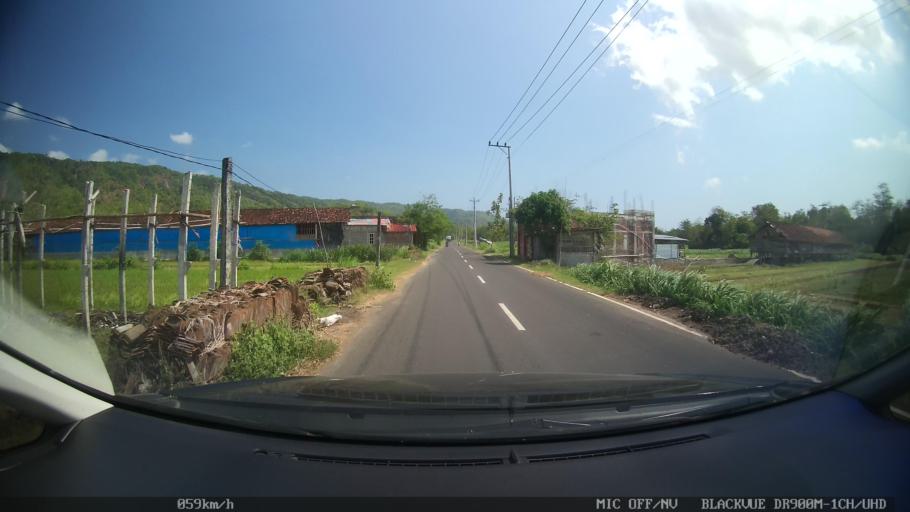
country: ID
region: Daerah Istimewa Yogyakarta
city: Pundong
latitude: -7.9690
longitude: 110.3521
